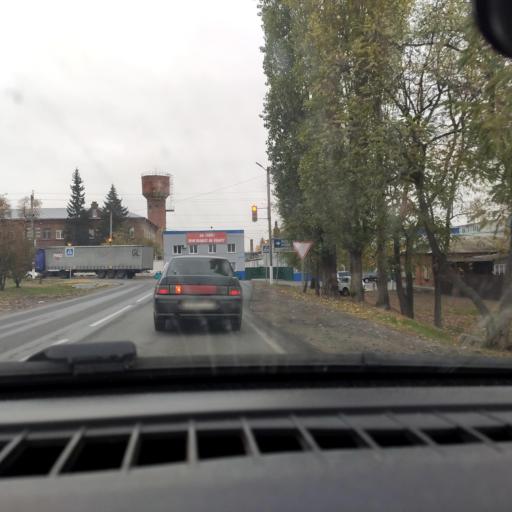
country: RU
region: Voronezj
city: Ostrogozhsk
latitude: 50.8681
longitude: 39.0750
